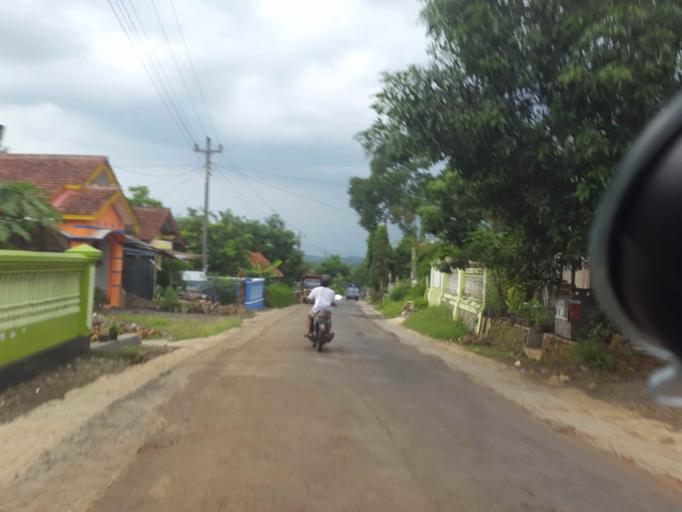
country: ID
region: Central Java
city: Banyumas
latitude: -7.5314
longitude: 109.3115
